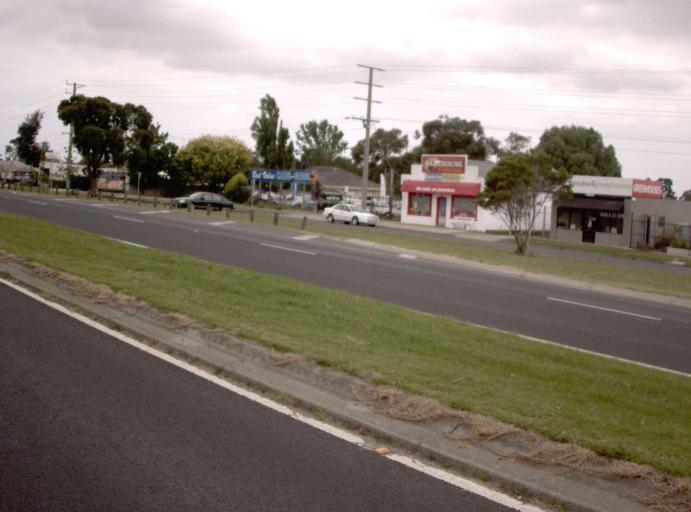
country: AU
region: Victoria
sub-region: Cardinia
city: Officer
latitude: -38.0596
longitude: 145.4071
